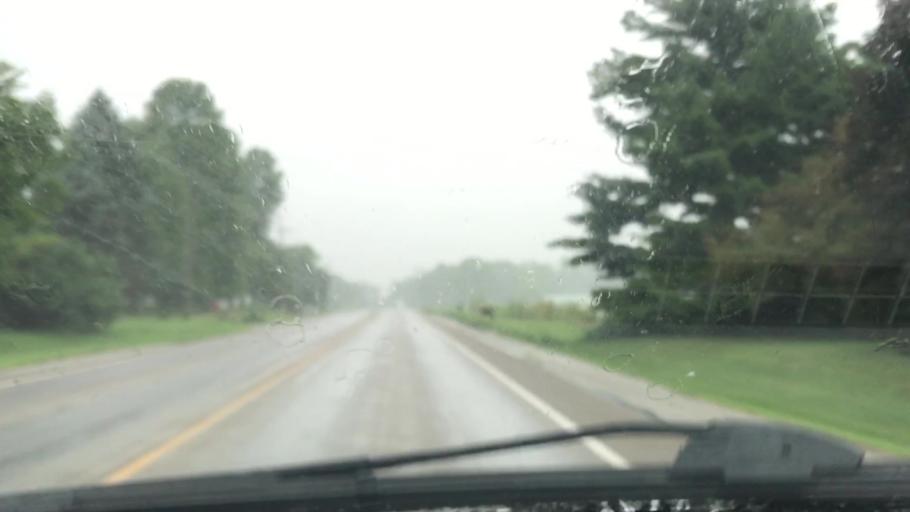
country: US
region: Indiana
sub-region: Hamilton County
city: Sheridan
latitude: 40.1230
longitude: -86.1941
